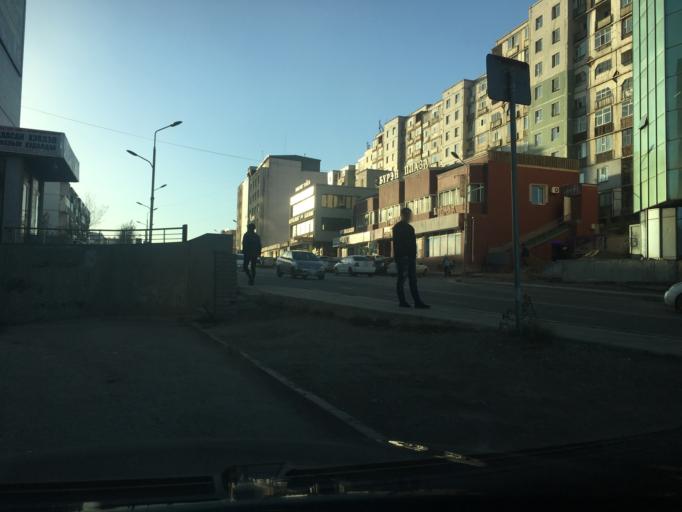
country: MN
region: Ulaanbaatar
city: Ulaanbaatar
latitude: 47.9251
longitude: 106.8822
